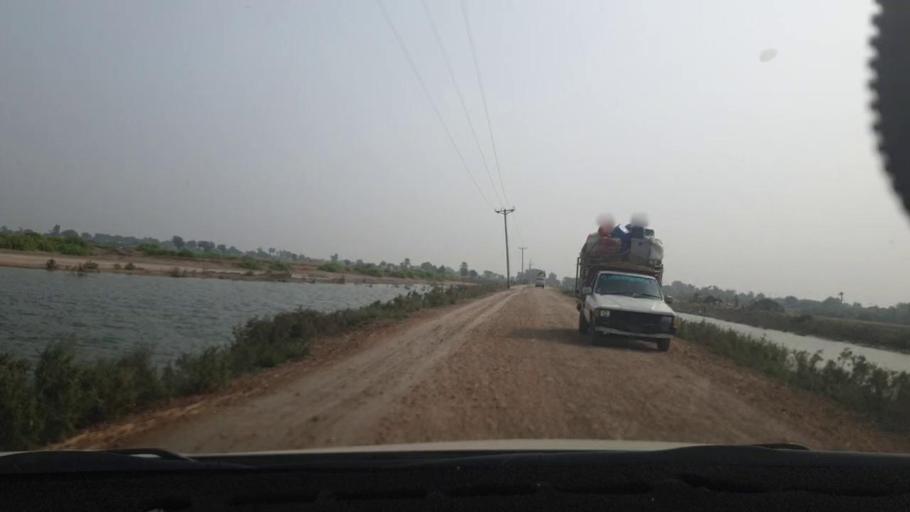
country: PK
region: Sindh
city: Tando Muhammad Khan
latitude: 25.0767
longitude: 68.4964
